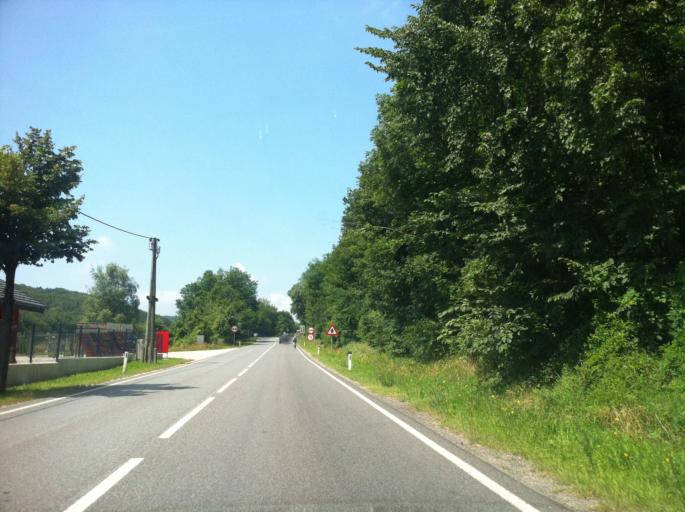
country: AT
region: Lower Austria
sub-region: Politischer Bezirk Wien-Umgebung
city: Gablitz
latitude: 48.2418
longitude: 16.1302
